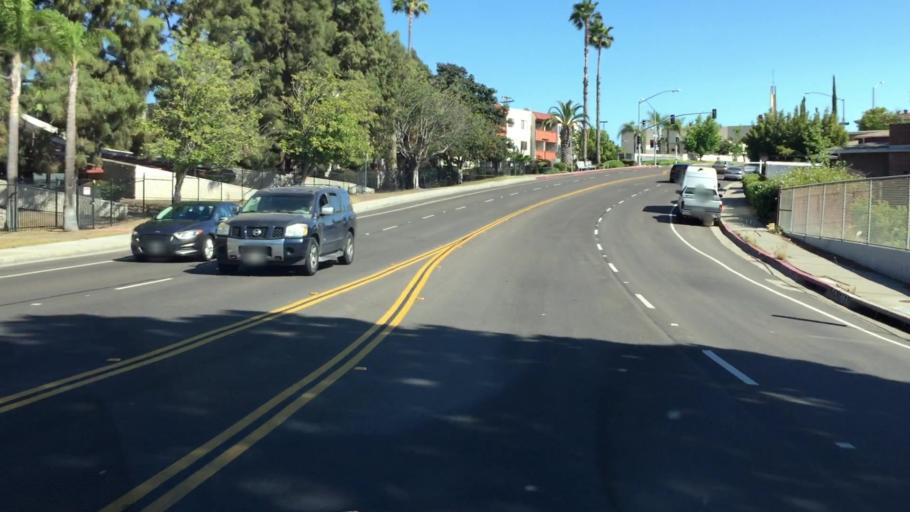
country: US
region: California
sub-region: San Diego County
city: Lemon Grove
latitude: 32.7664
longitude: -117.0672
